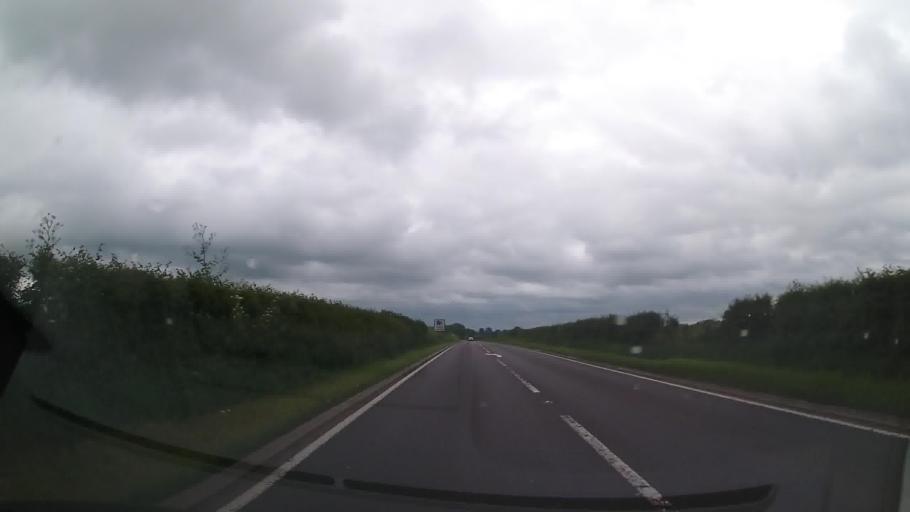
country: GB
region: England
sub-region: Shropshire
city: Prees
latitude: 52.9003
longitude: -2.6122
